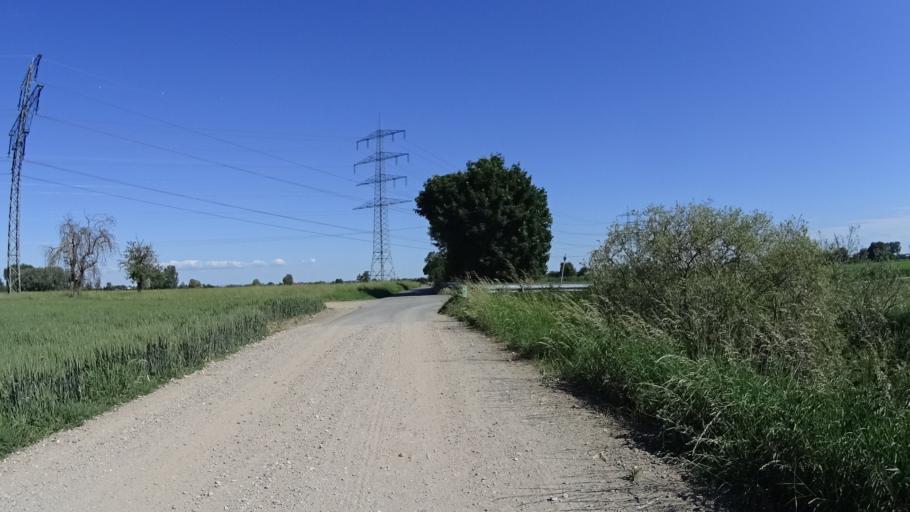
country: DE
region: Hesse
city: Pfungstadt
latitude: 49.7765
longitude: 8.5743
